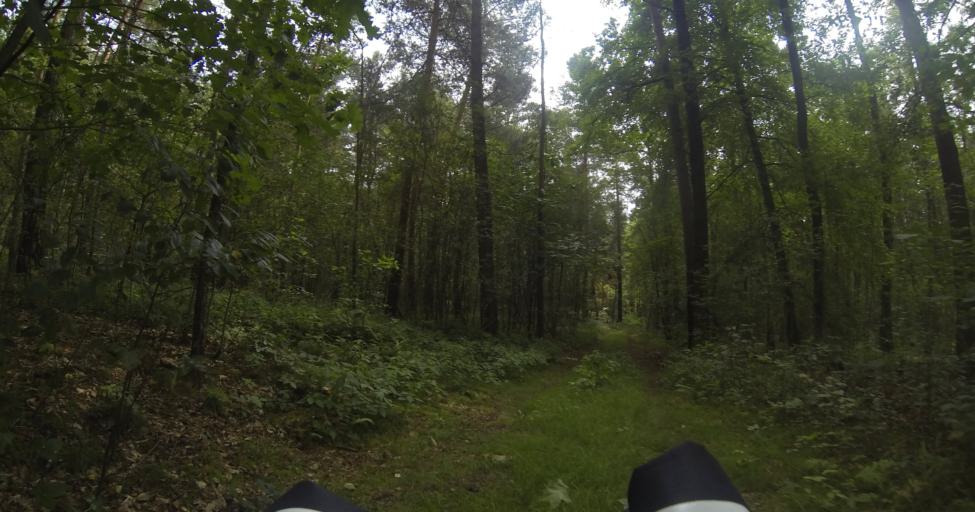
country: DE
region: Saxony
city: Weinbohla
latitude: 51.1926
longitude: 13.5990
